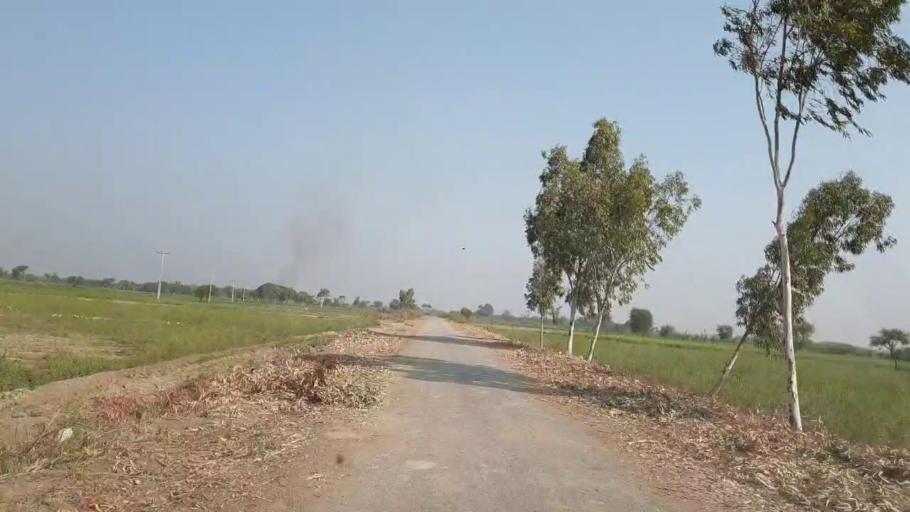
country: PK
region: Sindh
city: Mirpur Khas
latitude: 25.5861
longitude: 69.0022
